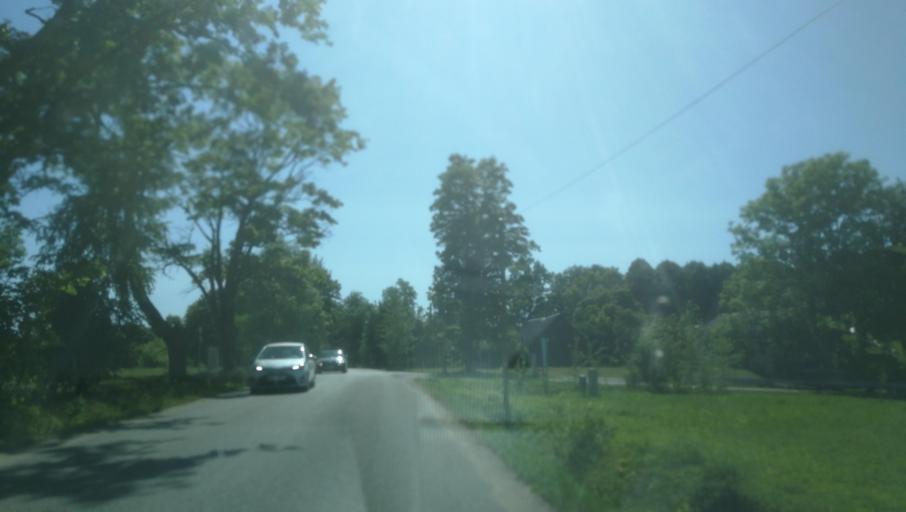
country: LV
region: Cesu Rajons
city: Cesis
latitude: 57.2964
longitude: 25.2361
